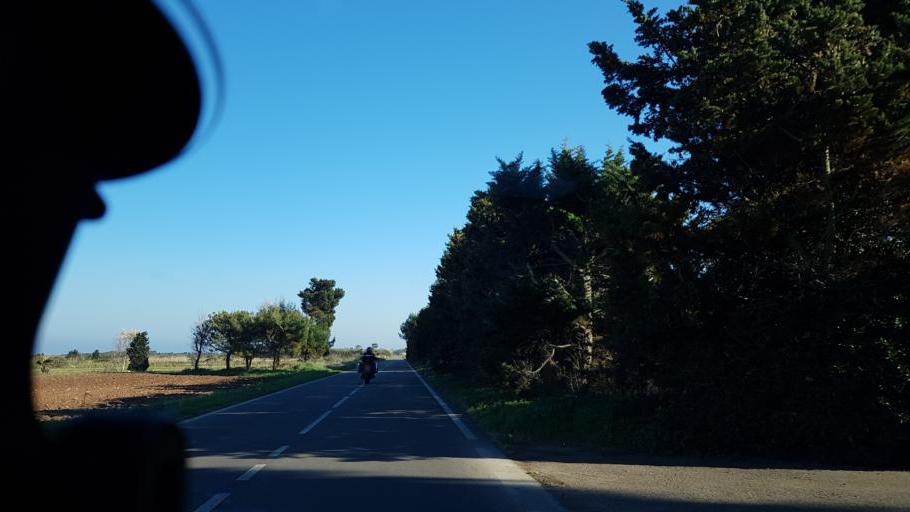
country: IT
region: Apulia
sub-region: Provincia di Lecce
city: Giorgilorio
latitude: 40.4418
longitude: 18.2334
